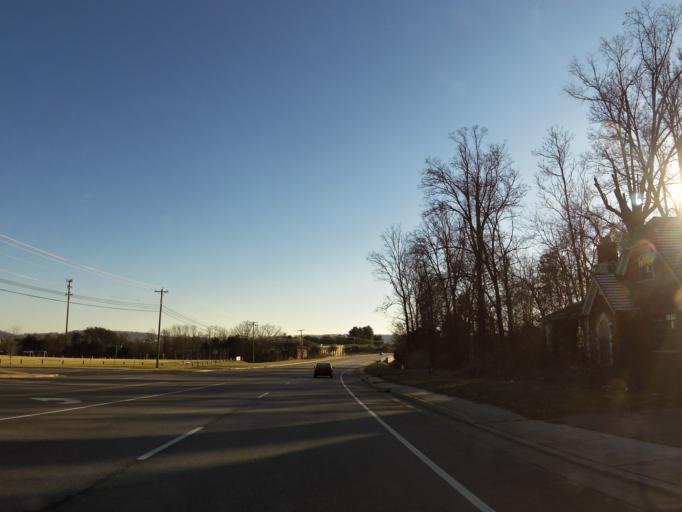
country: US
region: Tennessee
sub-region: Knox County
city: Farragut
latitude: 35.9197
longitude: -84.1489
